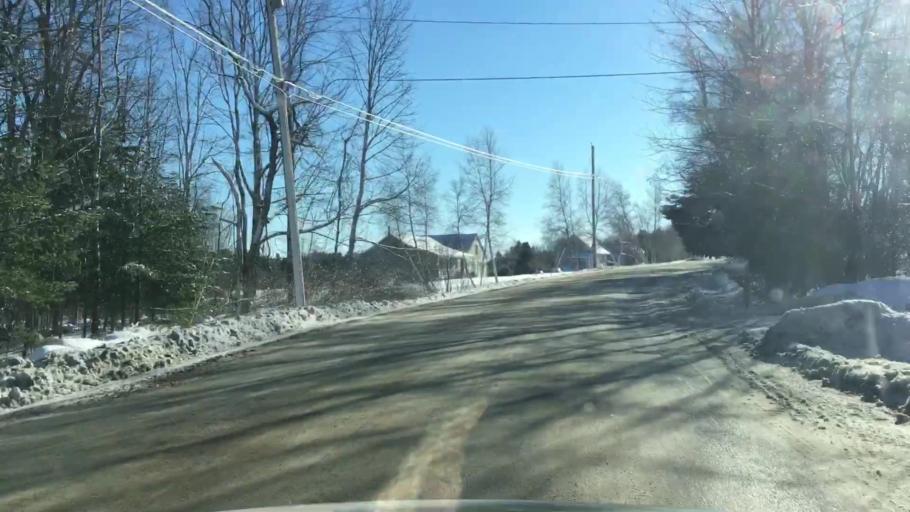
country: US
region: Maine
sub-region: Kennebec County
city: Winthrop
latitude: 44.3443
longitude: -69.9895
